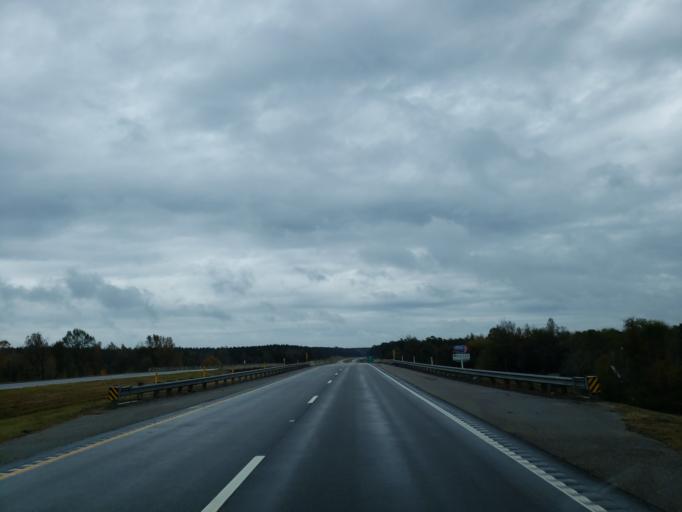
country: US
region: Mississippi
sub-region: Wayne County
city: Waynesboro
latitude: 31.6922
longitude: -88.6648
